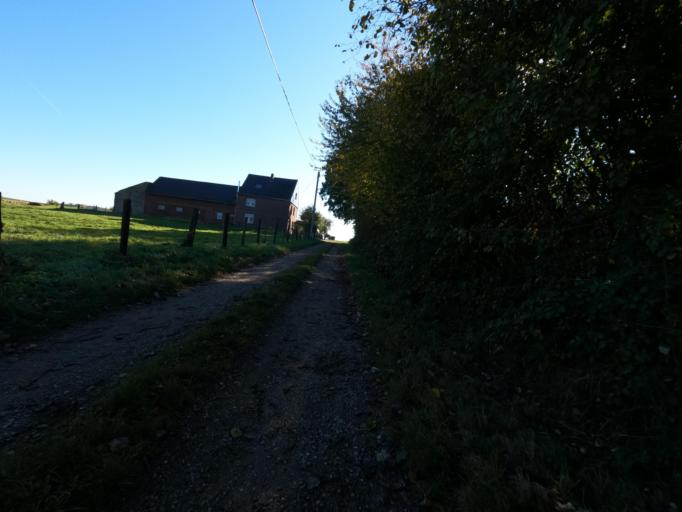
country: DE
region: North Rhine-Westphalia
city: Huckelhoven
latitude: 51.0478
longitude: 6.2579
